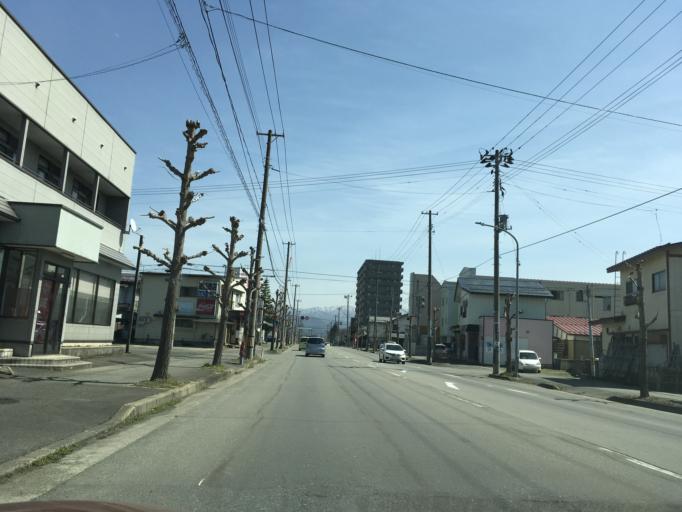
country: JP
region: Yamagata
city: Yonezawa
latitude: 37.9222
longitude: 140.1115
